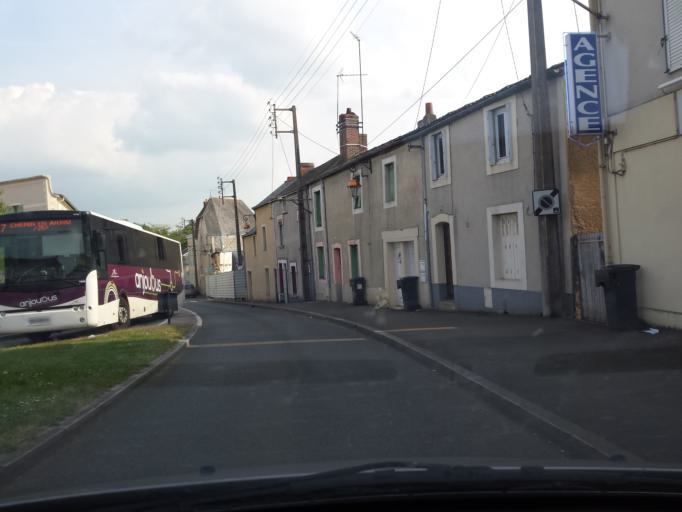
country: FR
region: Pays de la Loire
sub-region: Departement de Maine-et-Loire
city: Chemille-Melay
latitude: 47.2079
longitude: -0.7297
